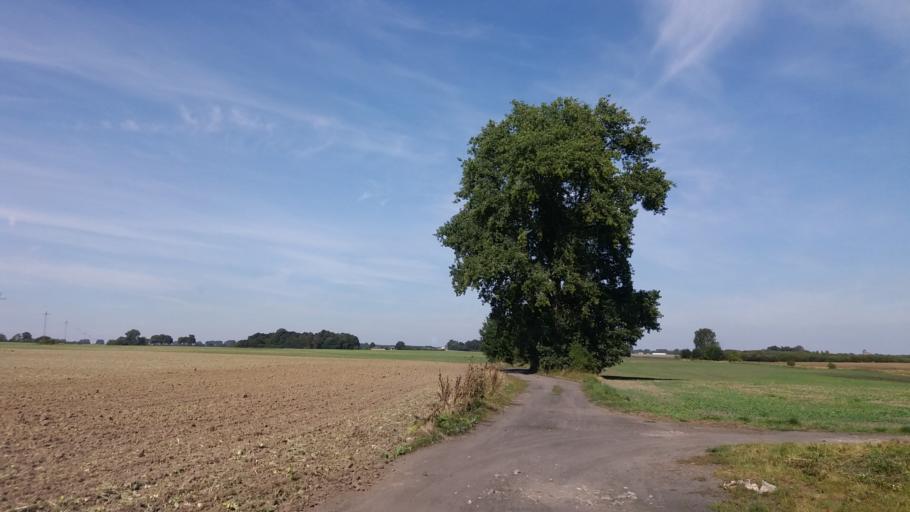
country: PL
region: West Pomeranian Voivodeship
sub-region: Powiat choszczenski
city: Choszczno
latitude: 53.1297
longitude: 15.4060
